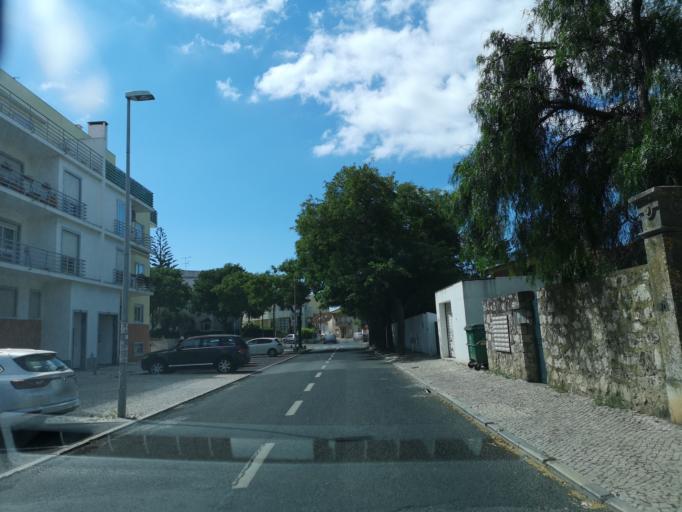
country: PT
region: Lisbon
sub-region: Oeiras
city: Oeiras
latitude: 38.6919
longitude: -9.3090
